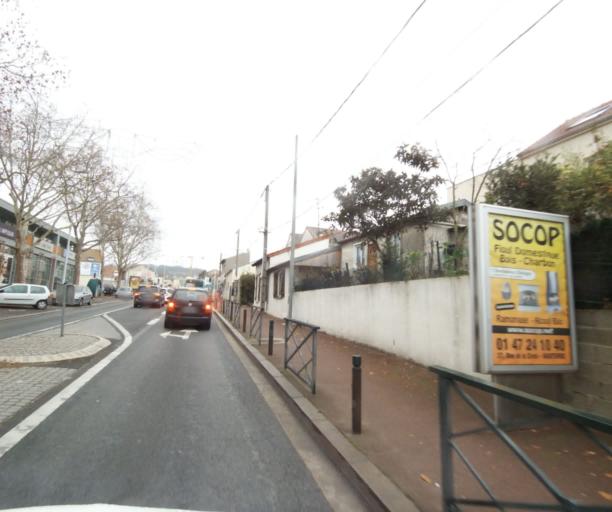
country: FR
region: Ile-de-France
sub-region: Departement des Hauts-de-Seine
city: Nanterre
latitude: 48.8831
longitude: 2.2040
